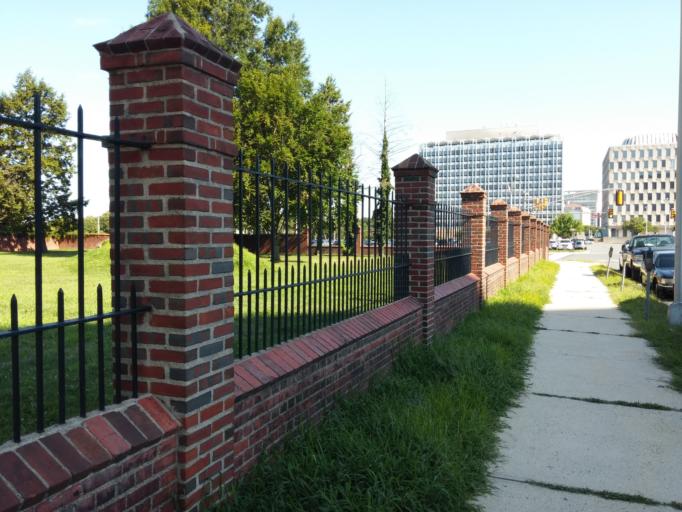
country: US
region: Pennsylvania
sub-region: Bucks County
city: Morrisville
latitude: 40.2131
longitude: -74.7654
